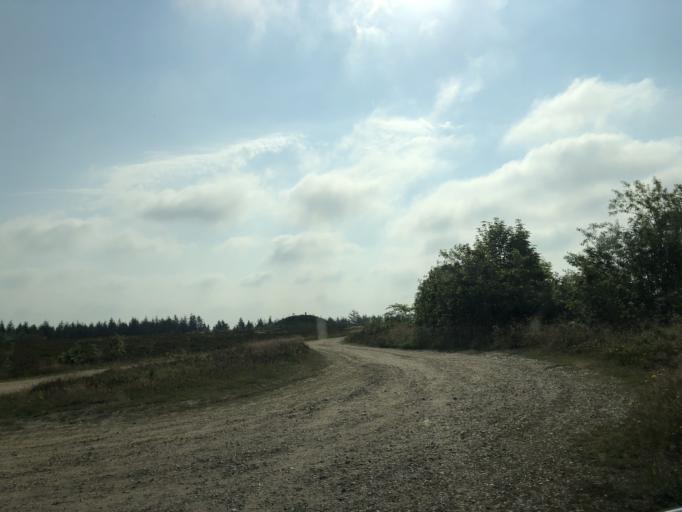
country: DK
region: Central Jutland
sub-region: Ringkobing-Skjern Kommune
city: Videbaek
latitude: 56.1569
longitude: 8.5168
